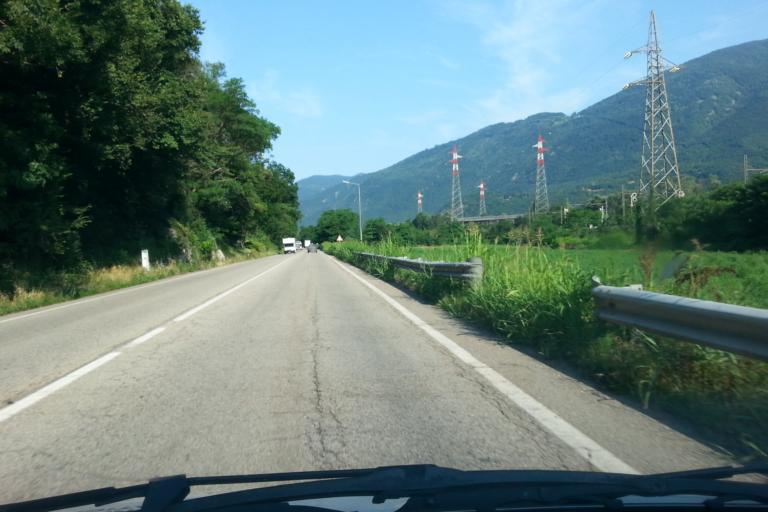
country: IT
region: Piedmont
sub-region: Provincia di Torino
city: Sant'Antonino di Susa
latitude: 45.1142
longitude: 7.2579
